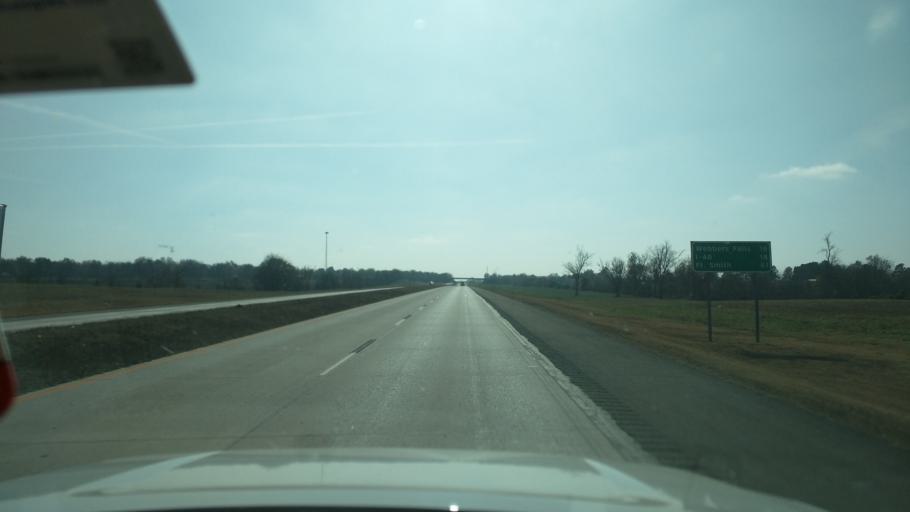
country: US
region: Oklahoma
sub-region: Muskogee County
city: Muskogee
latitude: 35.7069
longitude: -95.3098
